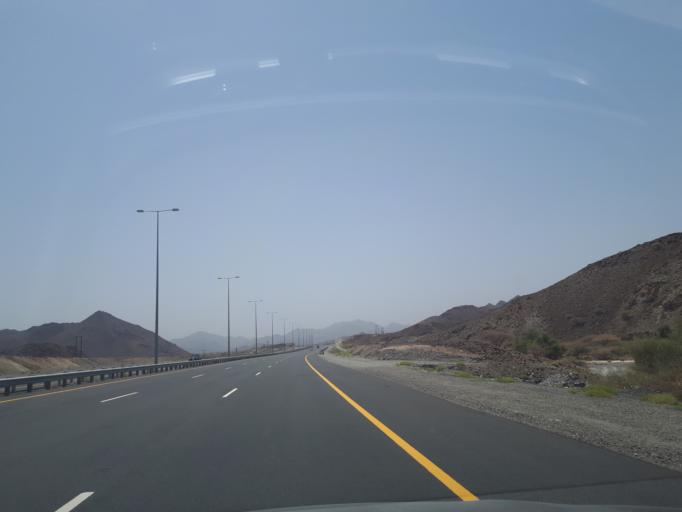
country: OM
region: Ash Sharqiyah
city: Ibra'
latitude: 22.8655
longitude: 58.3062
